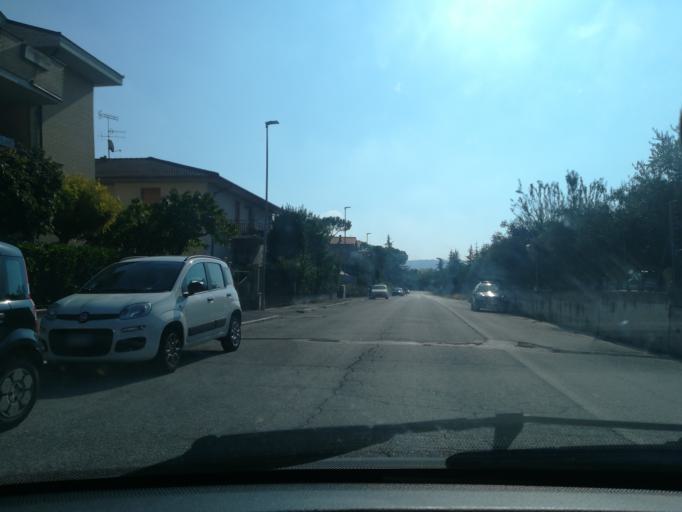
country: IT
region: The Marches
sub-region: Provincia di Macerata
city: Piediripa
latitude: 43.2756
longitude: 13.4755
